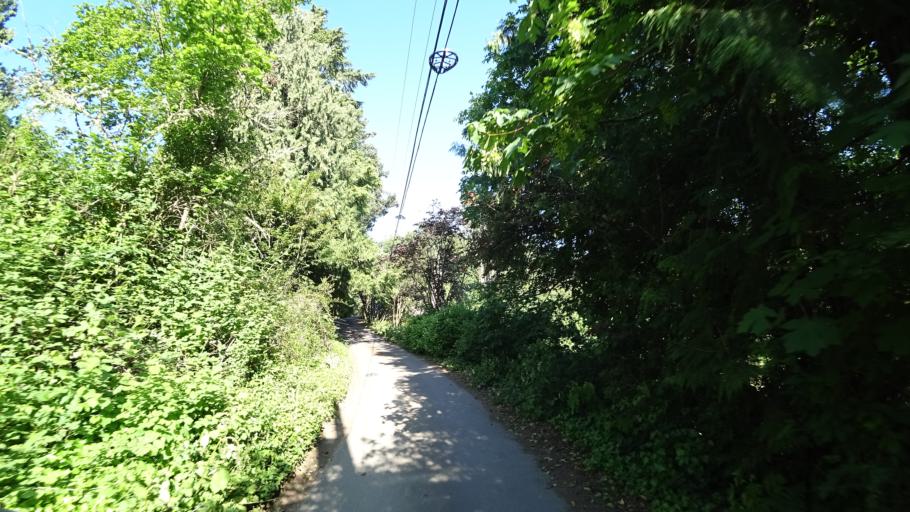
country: US
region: Oregon
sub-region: Clackamas County
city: Happy Valley
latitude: 45.4719
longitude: -122.5314
